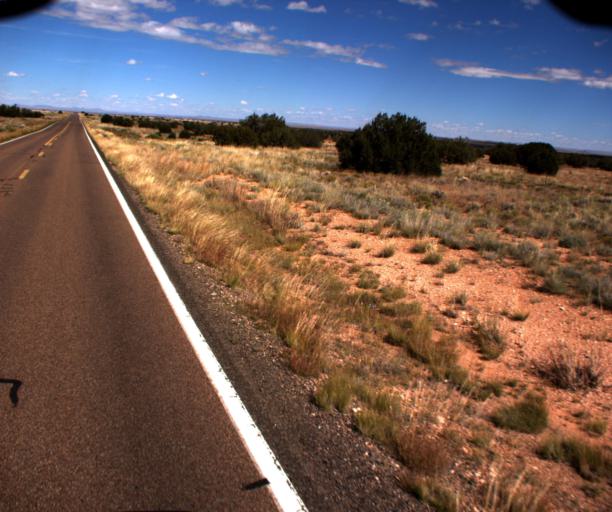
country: US
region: Arizona
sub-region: Navajo County
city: Holbrook
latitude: 34.7041
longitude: -110.3019
